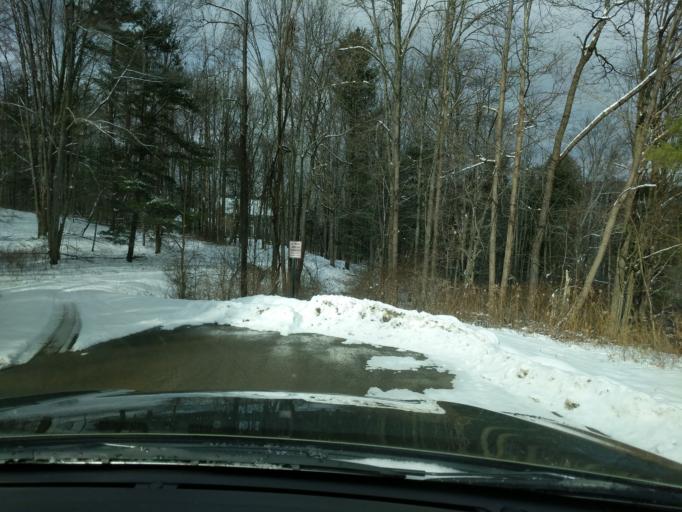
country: US
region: New York
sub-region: Tompkins County
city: Northeast Ithaca
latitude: 42.4303
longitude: -76.4002
